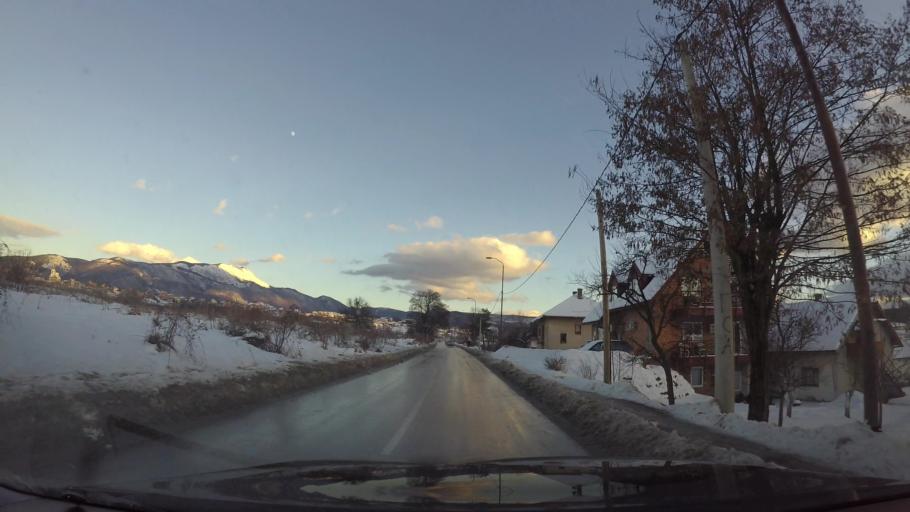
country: BA
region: Federation of Bosnia and Herzegovina
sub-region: Kanton Sarajevo
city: Sarajevo
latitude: 43.8156
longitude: 18.3624
